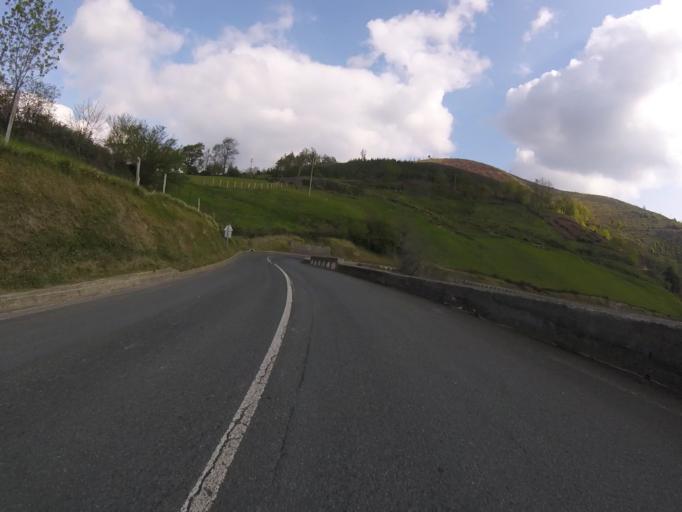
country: ES
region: Basque Country
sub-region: Provincia de Guipuzcoa
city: Elgoibar
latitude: 43.2025
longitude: -2.3607
